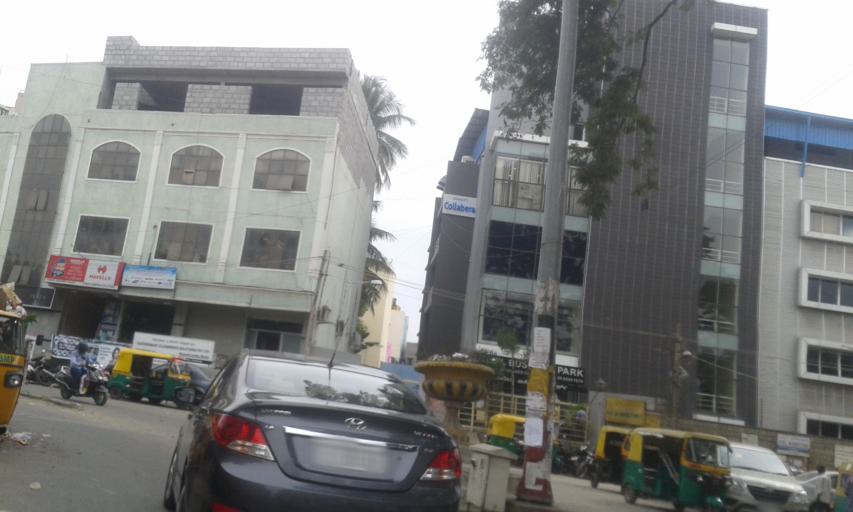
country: IN
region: Karnataka
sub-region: Bangalore Urban
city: Bangalore
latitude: 12.9515
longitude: 77.6076
